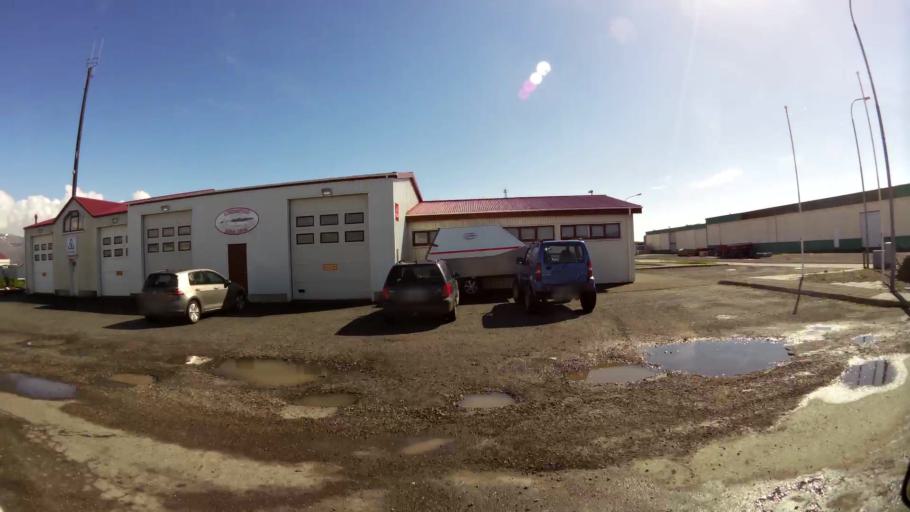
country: IS
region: East
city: Hoefn
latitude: 64.2520
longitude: -15.1995
